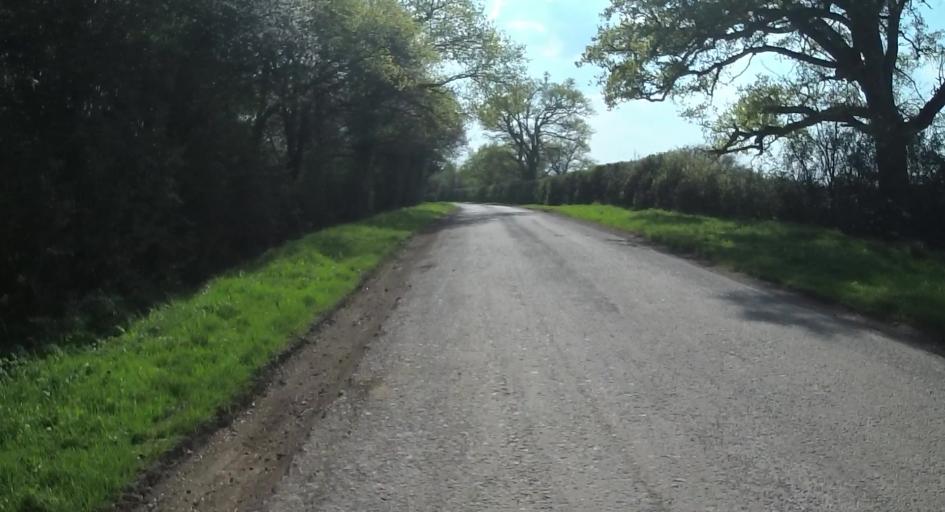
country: GB
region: England
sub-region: West Berkshire
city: Stratfield Mortimer
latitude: 51.3613
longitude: -1.0065
